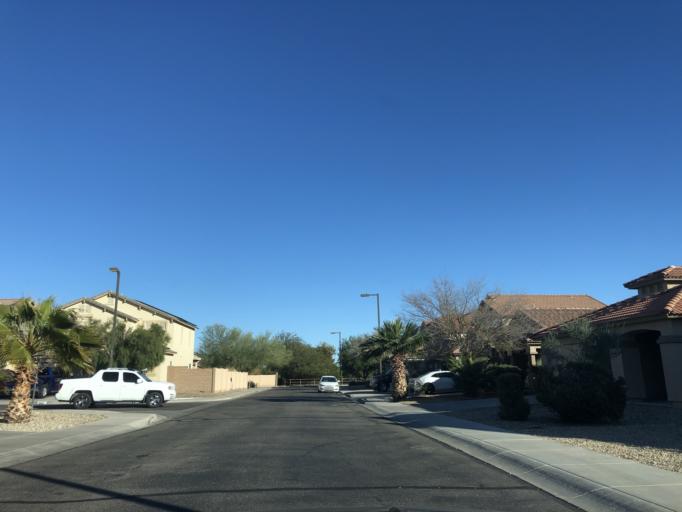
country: US
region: Arizona
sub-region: Maricopa County
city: Buckeye
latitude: 33.4367
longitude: -112.5726
